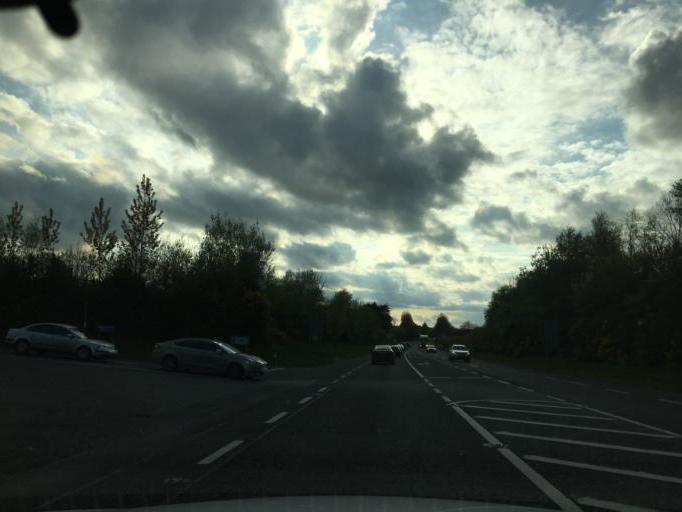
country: IE
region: Leinster
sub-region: Loch Garman
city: Loch Garman
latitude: 52.3383
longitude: -6.5463
